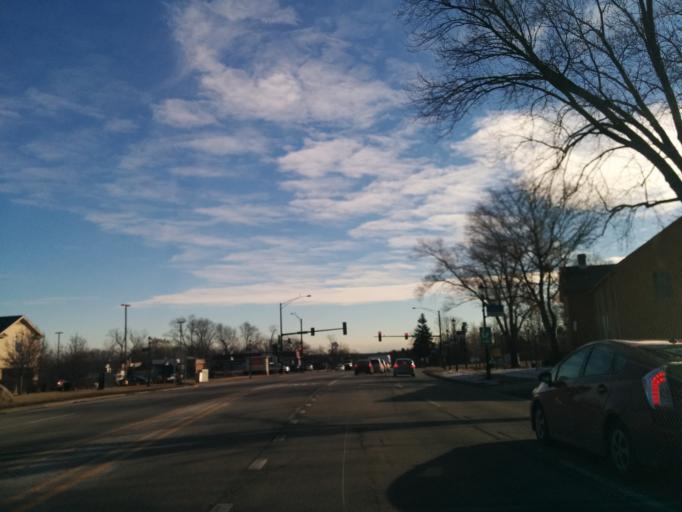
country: US
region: Illinois
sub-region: DuPage County
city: Glen Ellyn
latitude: 41.8899
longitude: -88.0652
